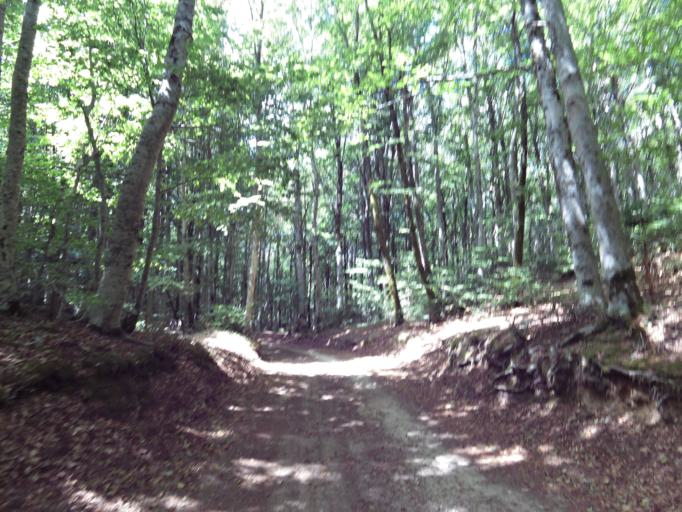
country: IT
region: Calabria
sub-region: Provincia di Vibo-Valentia
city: Mongiana
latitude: 38.5178
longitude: 16.3453
